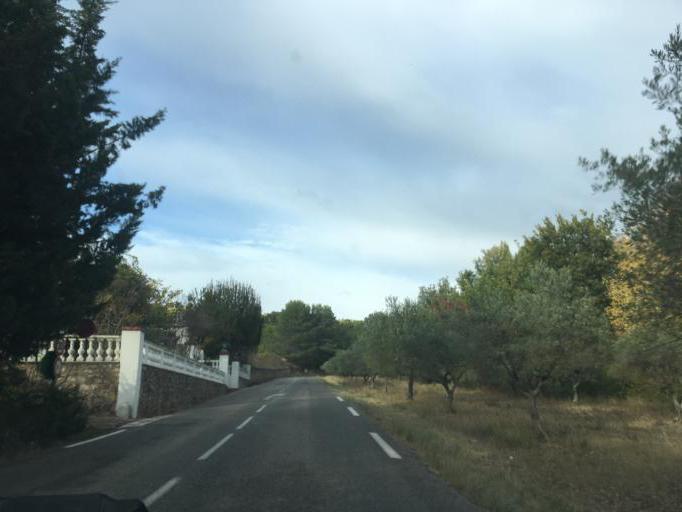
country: FR
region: Provence-Alpes-Cote d'Azur
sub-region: Departement du Var
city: Villecroze
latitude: 43.5785
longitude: 6.2664
